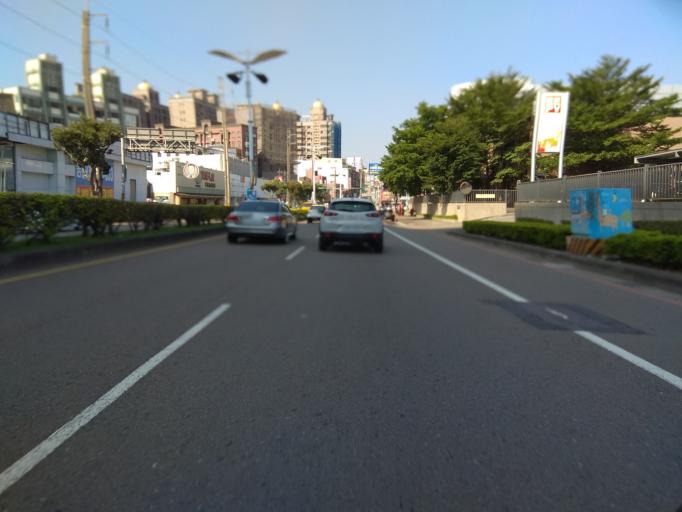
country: TW
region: Taiwan
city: Taoyuan City
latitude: 24.9661
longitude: 121.2373
